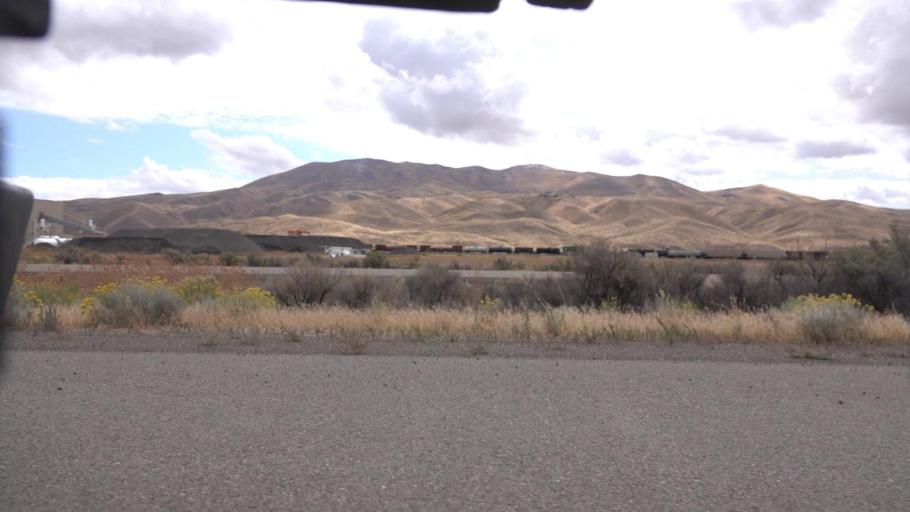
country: US
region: Nevada
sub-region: Elko County
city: Elko
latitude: 40.9383
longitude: -115.6553
